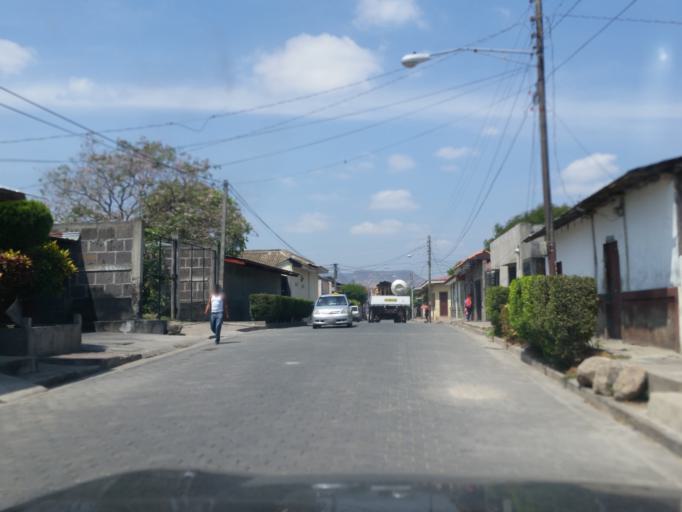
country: NI
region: Matagalpa
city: Ciudad Dario
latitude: 12.7293
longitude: -86.1223
